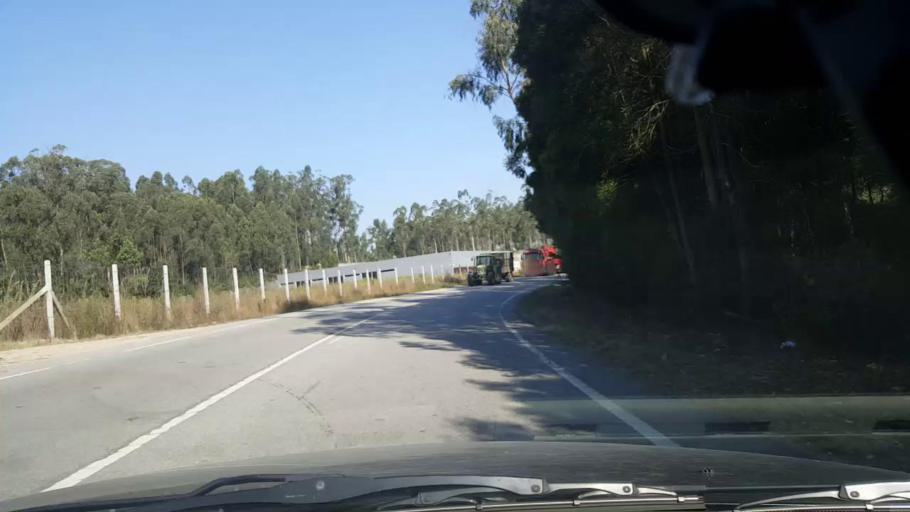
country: PT
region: Porto
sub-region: Vila do Conde
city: Arvore
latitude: 41.3545
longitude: -8.6878
